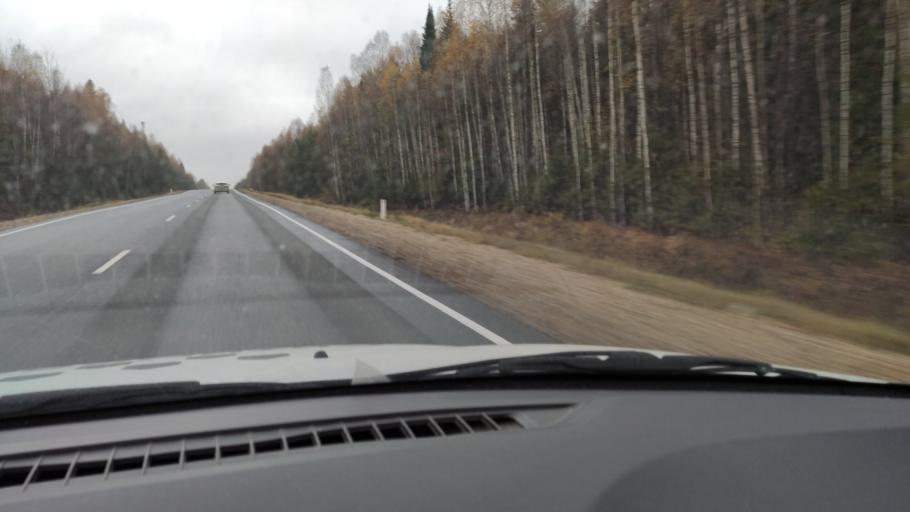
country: RU
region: Kirov
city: Chernaya Kholunitsa
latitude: 58.8591
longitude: 51.6818
